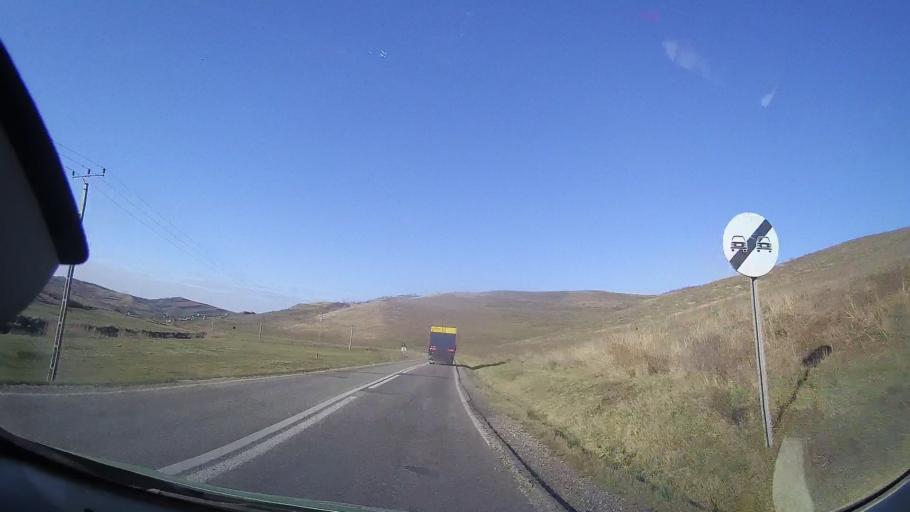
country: RO
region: Cluj
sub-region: Comuna Camarasu
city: Camarasu
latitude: 46.8019
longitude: 24.1606
